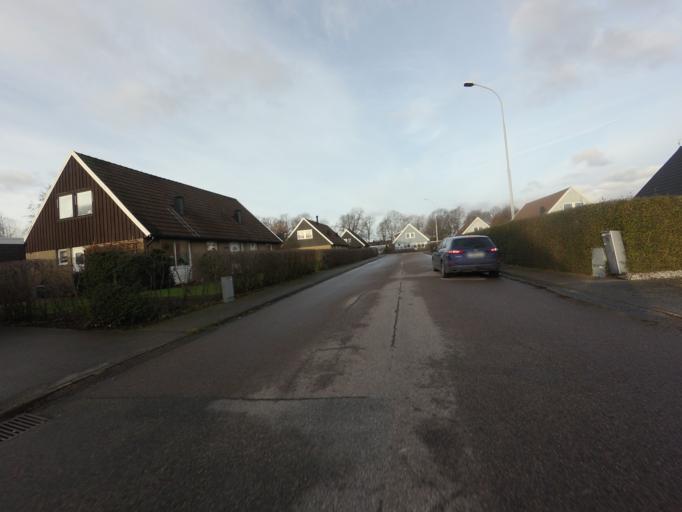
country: SE
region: Skane
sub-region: Hoganas Kommun
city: Hoganas
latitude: 56.1916
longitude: 12.5820
